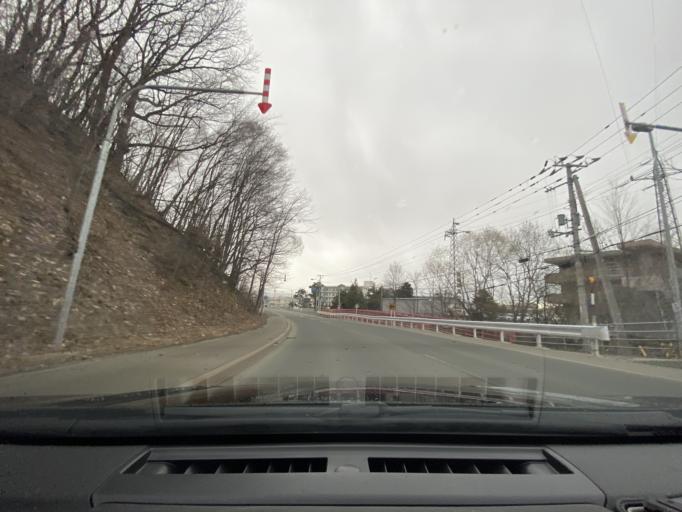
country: JP
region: Hokkaido
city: Kitami
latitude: 43.7967
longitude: 143.9167
